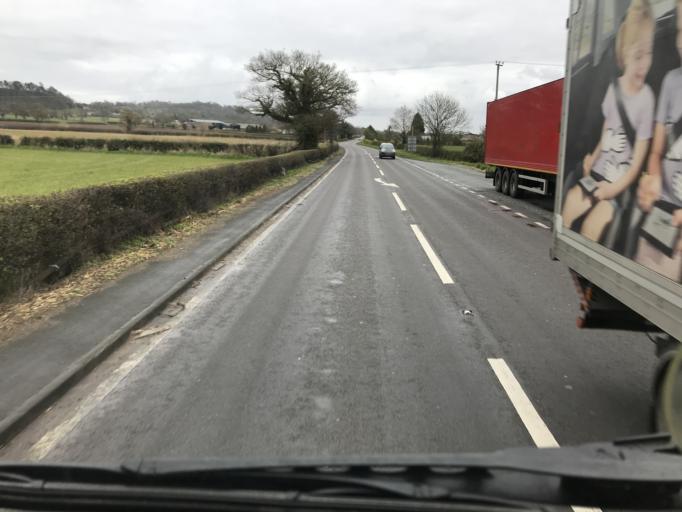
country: GB
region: England
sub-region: Cheshire West and Chester
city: Tattenhall
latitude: 53.0985
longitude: -2.7762
